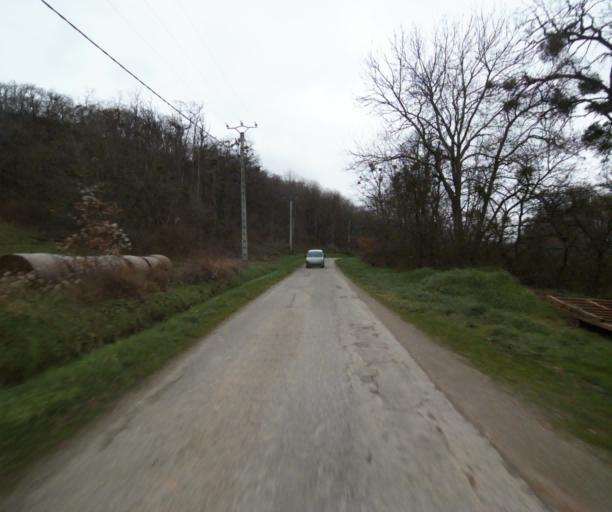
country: FR
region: Midi-Pyrenees
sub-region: Departement de l'Ariege
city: Saverdun
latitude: 43.2213
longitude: 1.5874
